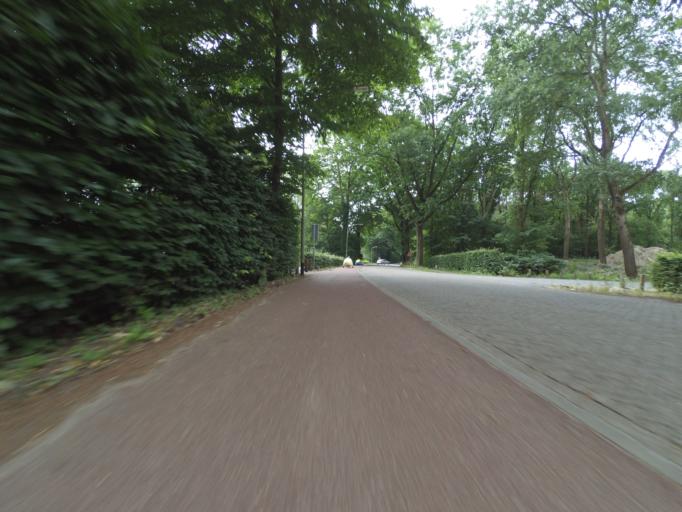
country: NL
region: North Brabant
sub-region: Gemeente Rucphen
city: Rucphen
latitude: 51.5709
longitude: 4.5600
